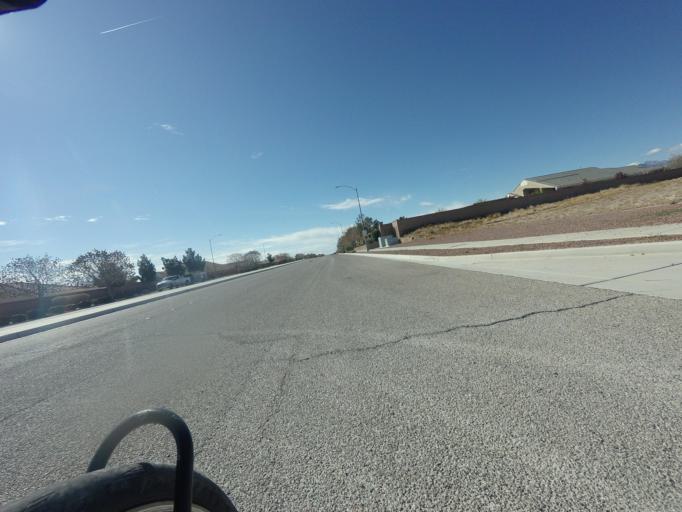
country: US
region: Nevada
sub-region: Clark County
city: North Las Vegas
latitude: 36.3352
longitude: -115.2788
